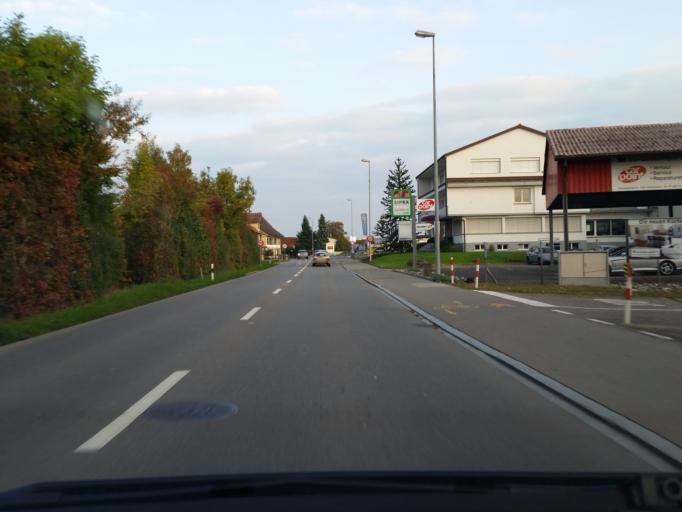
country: CH
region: Thurgau
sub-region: Arbon District
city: Salmsach
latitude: 47.5740
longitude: 9.3611
